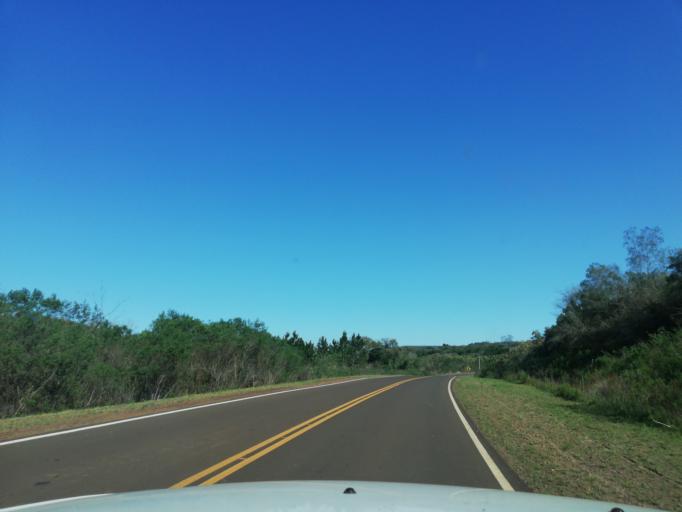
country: AR
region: Misiones
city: Arroyo del Medio
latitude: -27.6845
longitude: -55.3973
